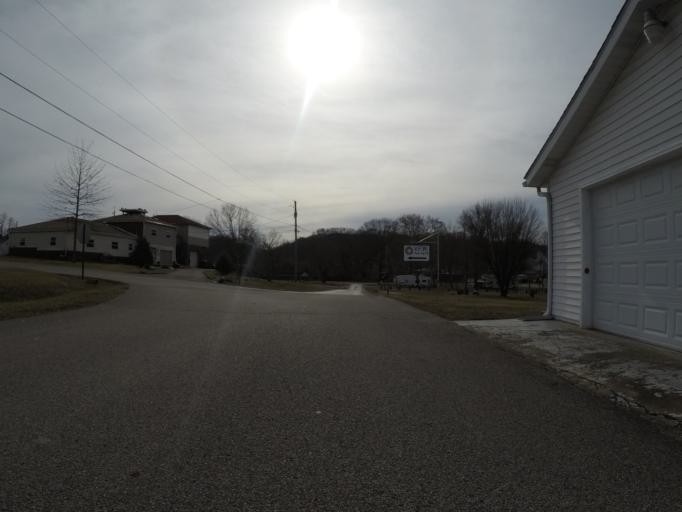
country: US
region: West Virginia
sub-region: Cabell County
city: Pea Ridge
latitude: 38.4405
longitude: -82.3651
